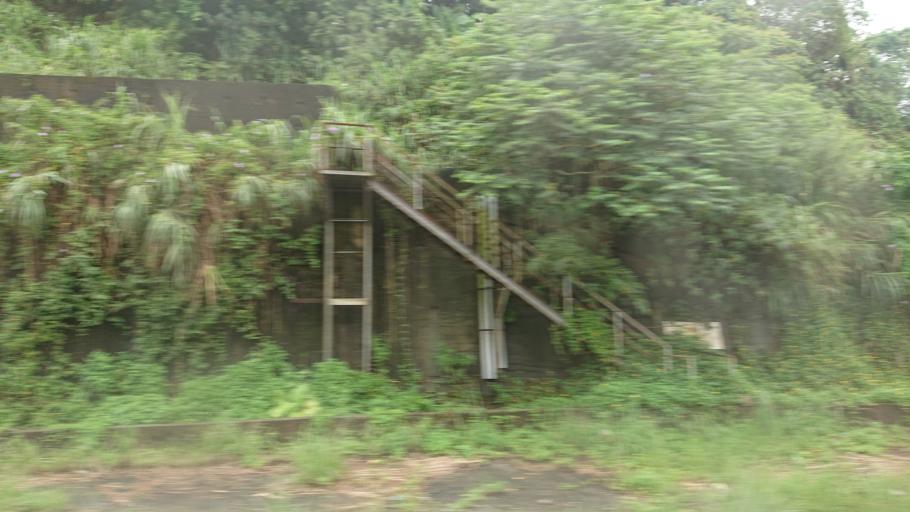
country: TW
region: Taiwan
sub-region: Keelung
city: Keelung
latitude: 25.0967
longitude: 121.7189
